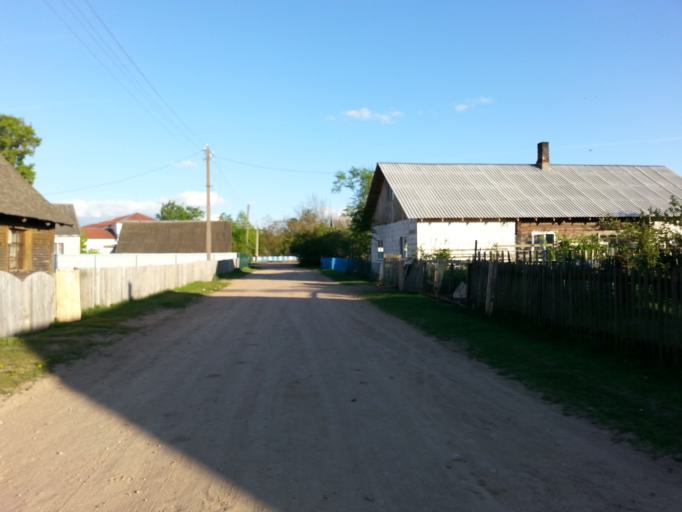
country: BY
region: Minsk
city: Narach
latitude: 54.9313
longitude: 26.6836
